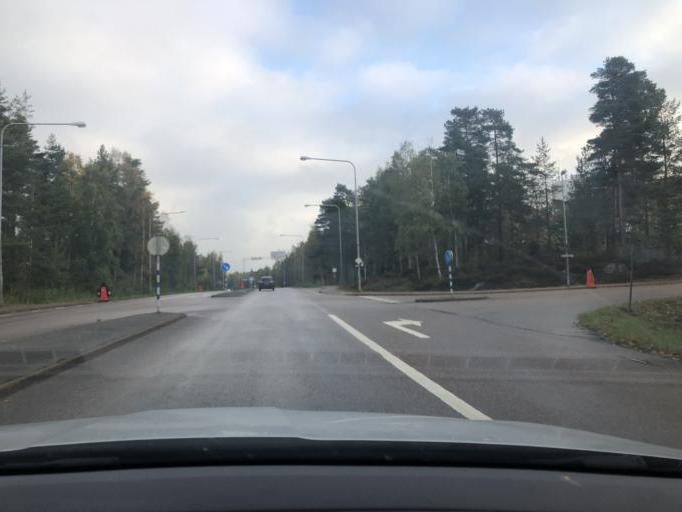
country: SE
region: Vaestra Goetaland
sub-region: Trollhattan
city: Trollhattan
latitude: 58.3157
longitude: 12.2703
